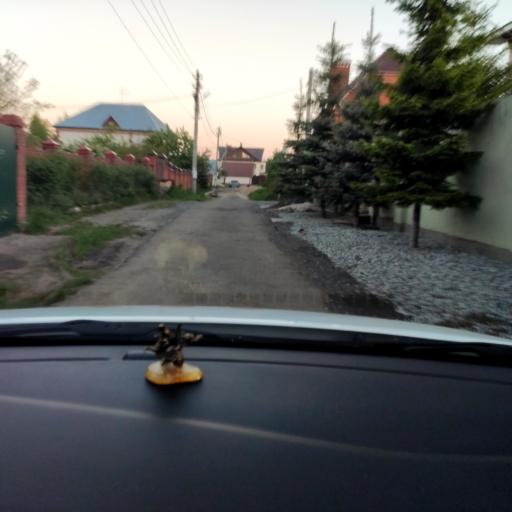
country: RU
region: Tatarstan
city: Stolbishchi
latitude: 55.7407
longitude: 49.2322
